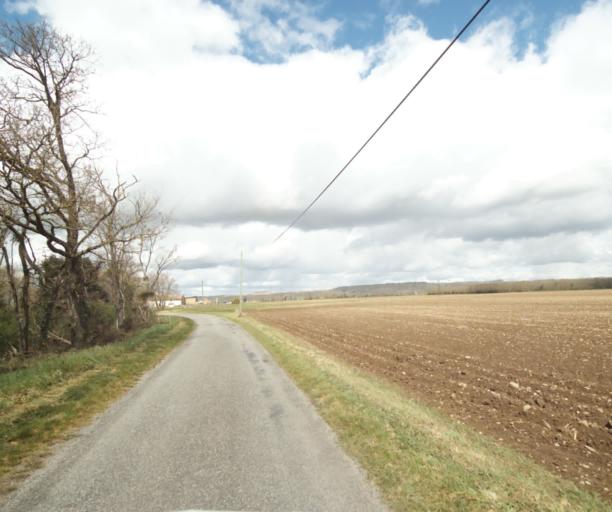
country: FR
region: Midi-Pyrenees
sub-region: Departement de l'Ariege
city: Saverdun
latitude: 43.2700
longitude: 1.5826
